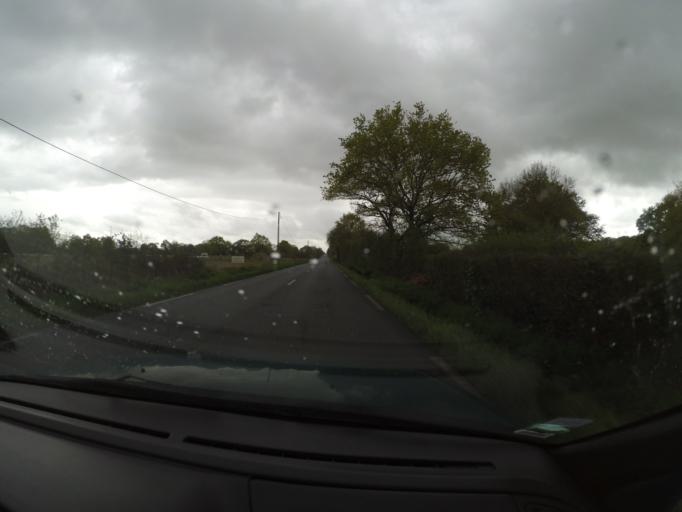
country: FR
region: Pays de la Loire
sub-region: Departement de la Loire-Atlantique
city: Vallet
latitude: 47.1900
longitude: -1.2528
